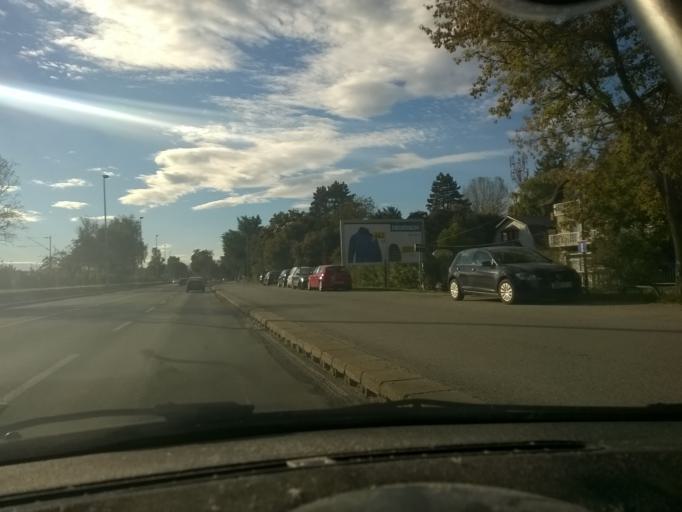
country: HR
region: Zagrebacka
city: Bestovje
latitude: 45.8152
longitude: 15.8467
